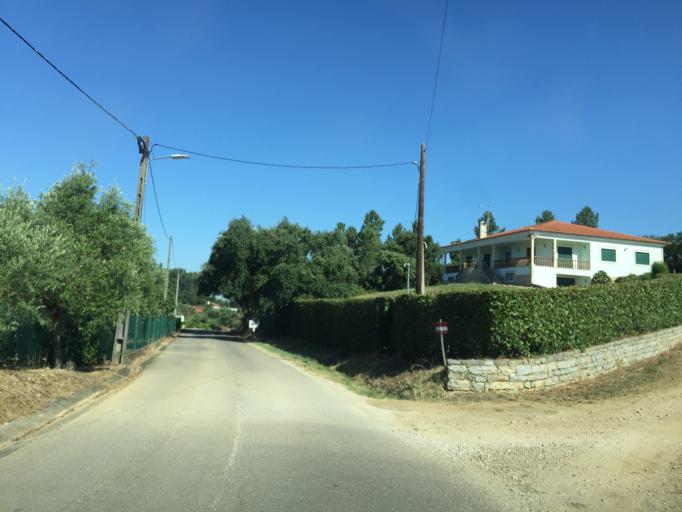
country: PT
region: Santarem
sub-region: Tomar
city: Tomar
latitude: 39.6037
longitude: -8.3273
